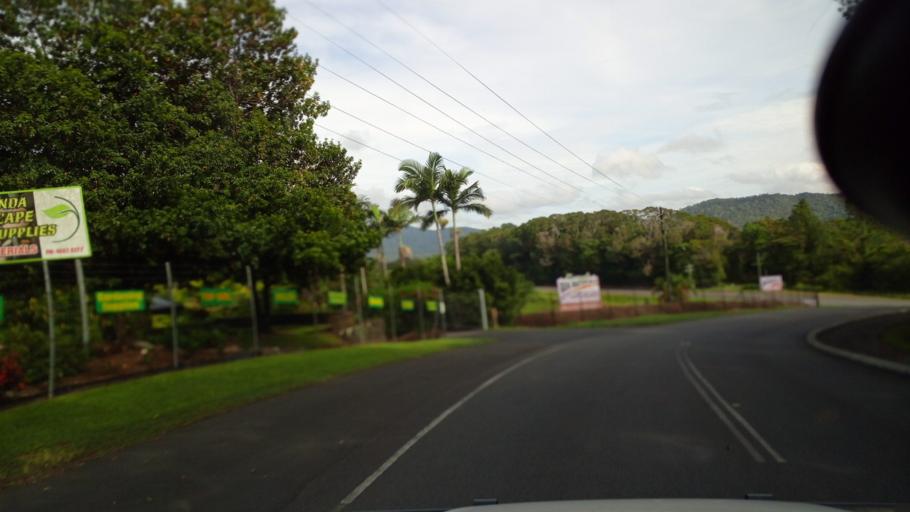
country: AU
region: Queensland
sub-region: Tablelands
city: Kuranda
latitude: -16.8204
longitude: 145.6233
